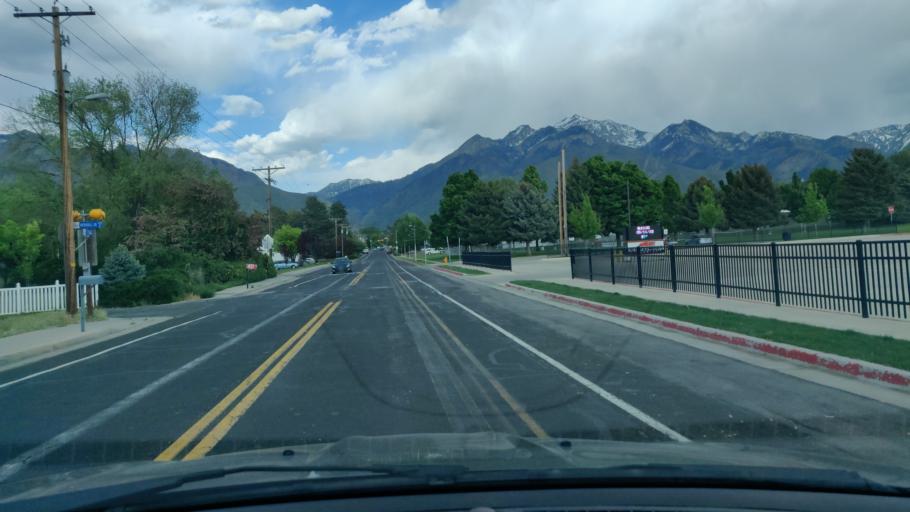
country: US
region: Utah
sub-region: Salt Lake County
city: Little Cottonwood Creek Valley
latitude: 40.6204
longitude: -111.8405
